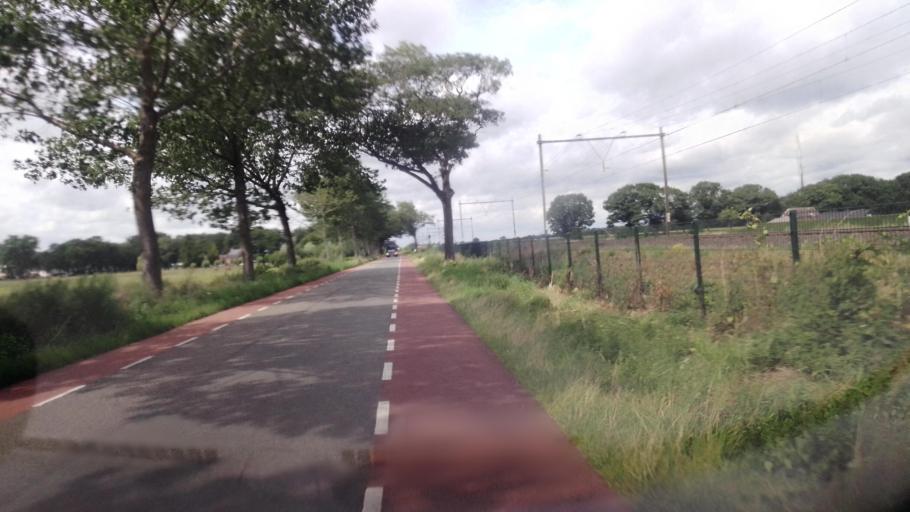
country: NL
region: North Brabant
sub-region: Gemeente Asten
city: Asten
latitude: 51.4466
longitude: 5.8697
